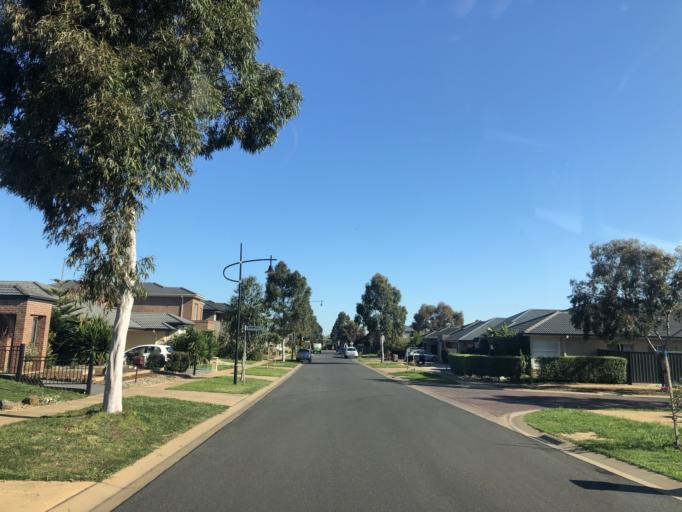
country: AU
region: Victoria
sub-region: Wyndham
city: Hoppers Crossing
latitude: -37.8930
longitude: 144.7194
